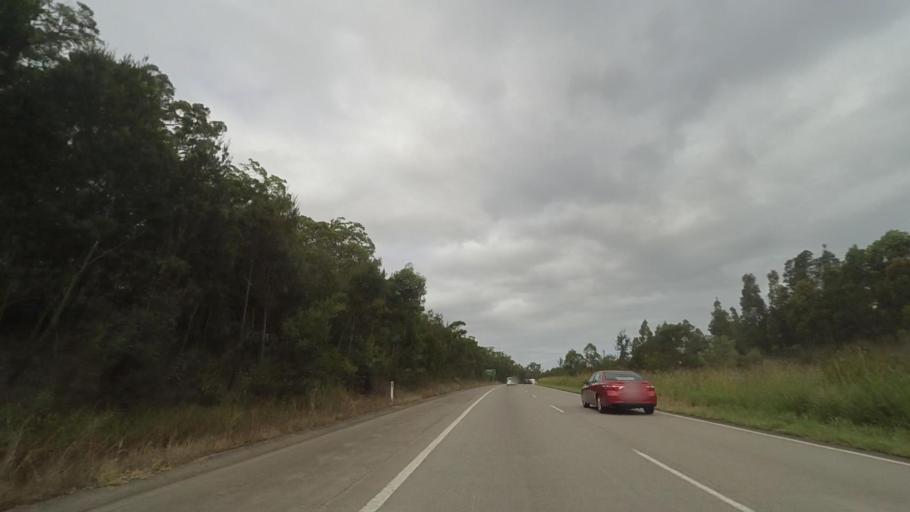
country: AU
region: New South Wales
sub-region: Port Stephens Shire
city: Port Stephens
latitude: -32.6340
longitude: 152.0145
